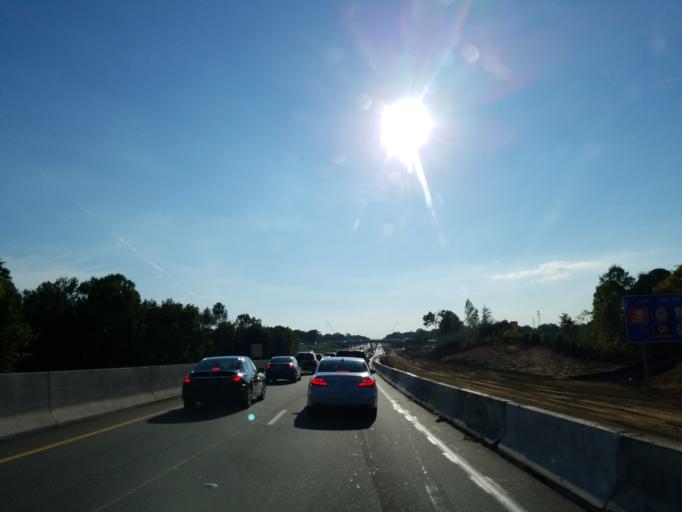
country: US
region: North Carolina
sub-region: Cabarrus County
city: Kannapolis
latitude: 35.4481
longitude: -80.6017
